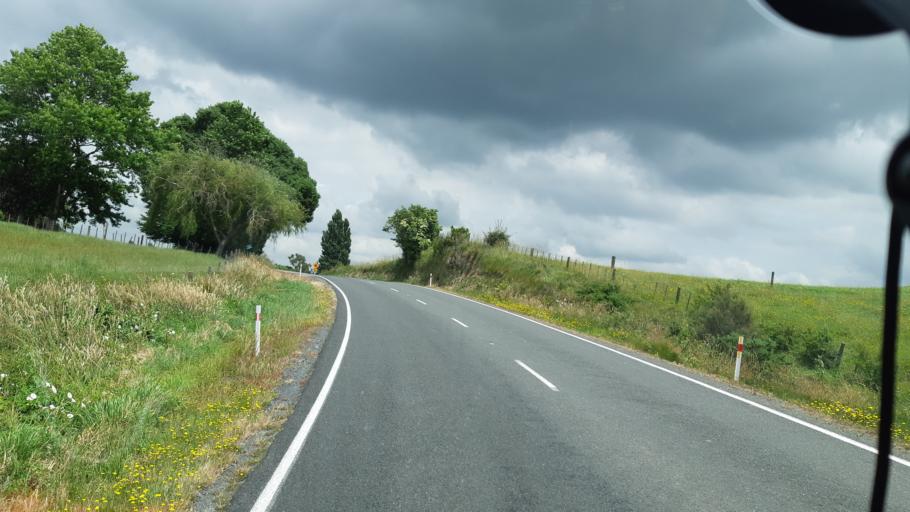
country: NZ
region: Waikato
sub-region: Waipa District
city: Cambridge
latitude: -38.1458
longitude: 175.5520
